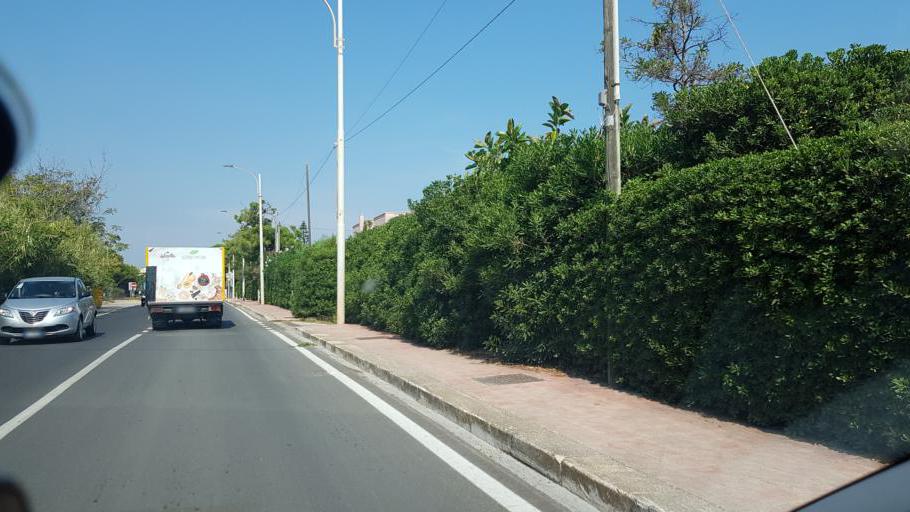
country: IT
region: Apulia
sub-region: Provincia di Brindisi
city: Fasano
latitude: 40.9041
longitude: 17.3522
